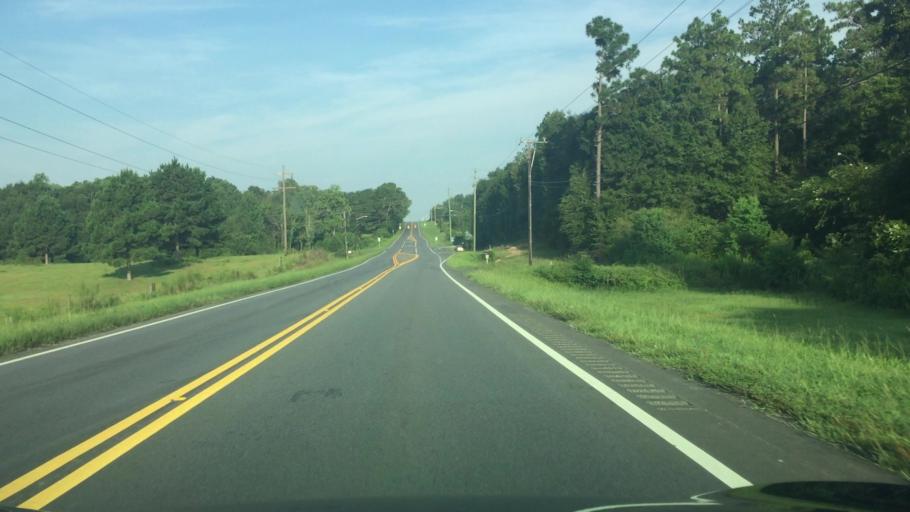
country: US
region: Alabama
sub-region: Covington County
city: Andalusia
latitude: 31.2781
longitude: -86.4953
